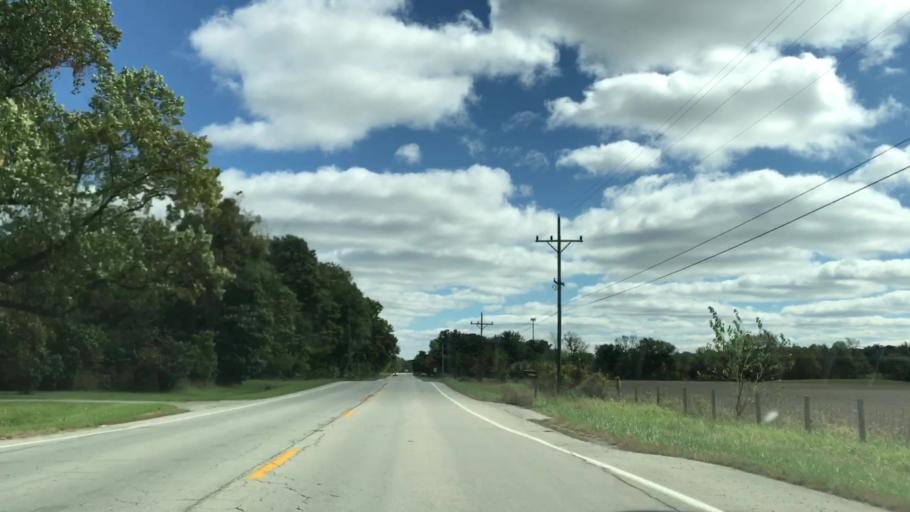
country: US
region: Indiana
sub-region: Hamilton County
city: Westfield
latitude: 40.0860
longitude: -86.1087
